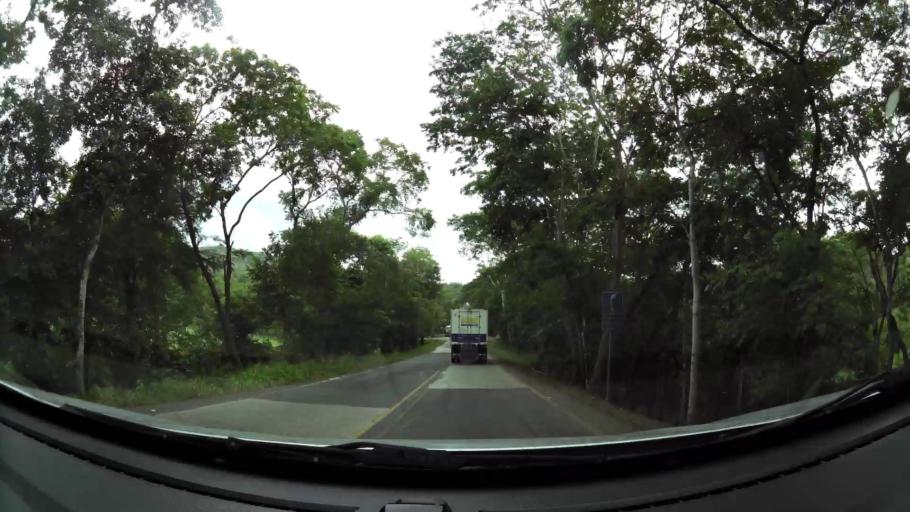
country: CR
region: Guanacaste
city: Juntas
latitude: 10.1646
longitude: -84.9192
